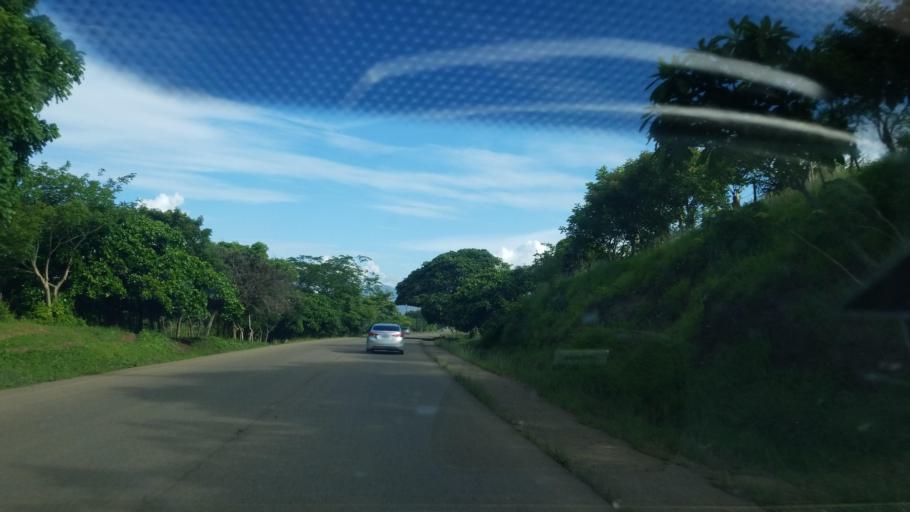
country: HN
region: El Paraiso
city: Arauli
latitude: 13.9414
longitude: -86.5588
